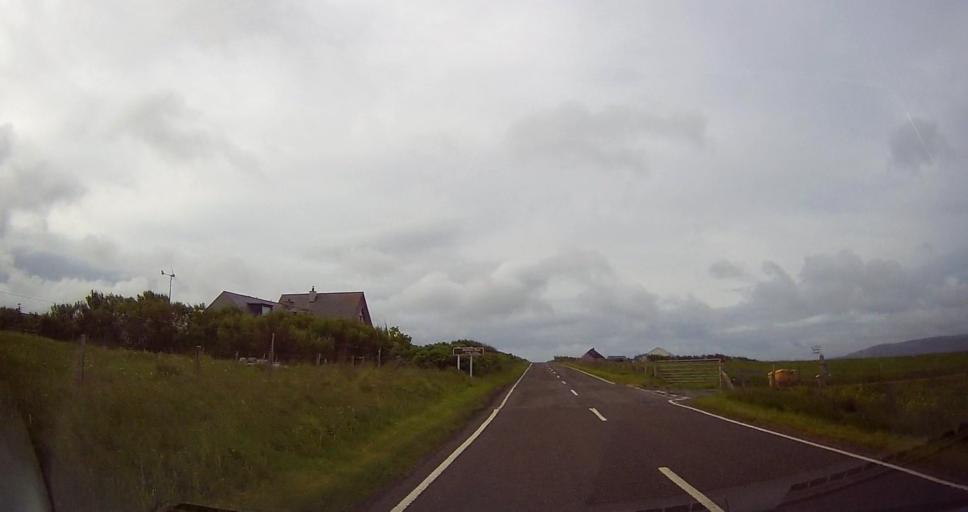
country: GB
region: Scotland
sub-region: Orkney Islands
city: Stromness
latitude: 58.9556
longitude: -3.2196
